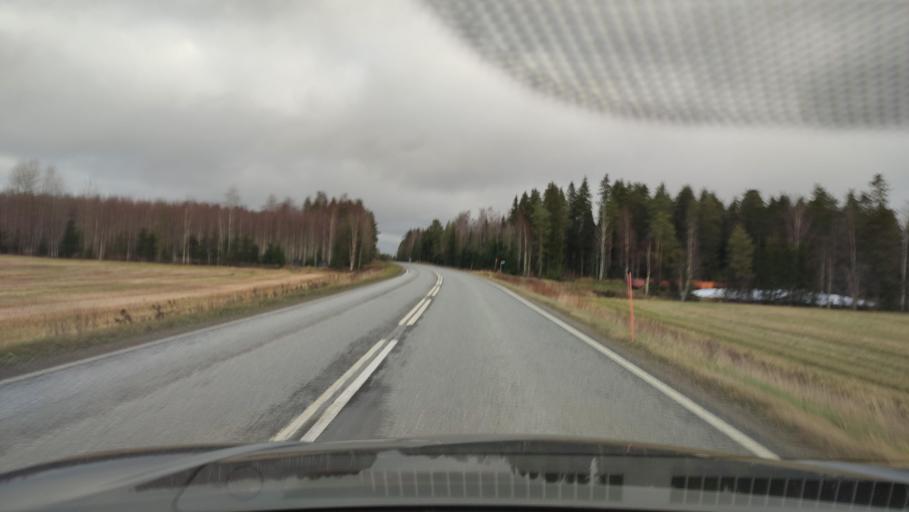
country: FI
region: Southern Ostrobothnia
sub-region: Suupohja
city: Kauhajoki
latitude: 62.3856
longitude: 22.1394
